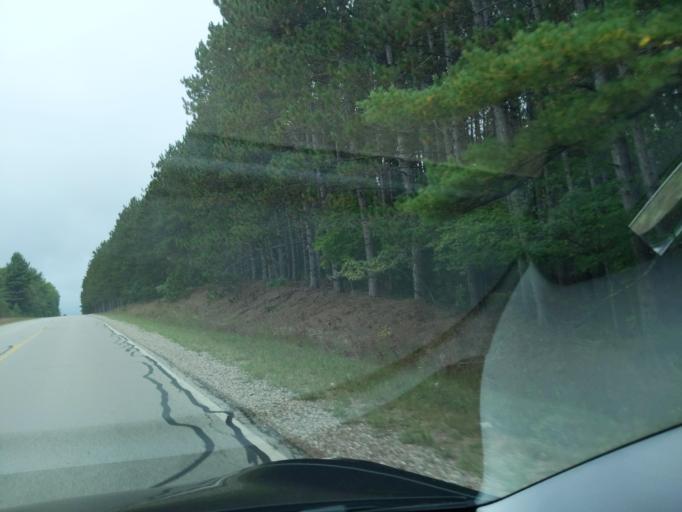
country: US
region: Michigan
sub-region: Grand Traverse County
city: Kingsley
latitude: 44.6207
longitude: -85.3532
